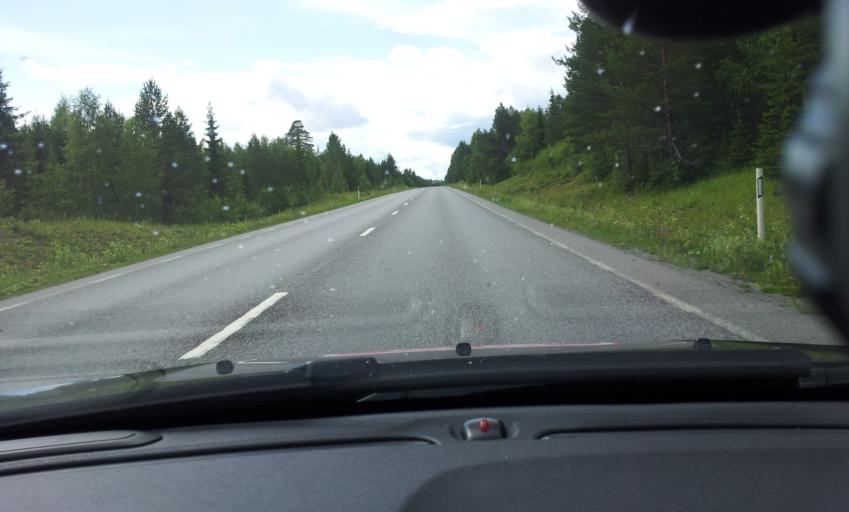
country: SE
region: Jaemtland
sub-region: Krokoms Kommun
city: Krokom
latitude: 63.3132
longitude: 14.1236
